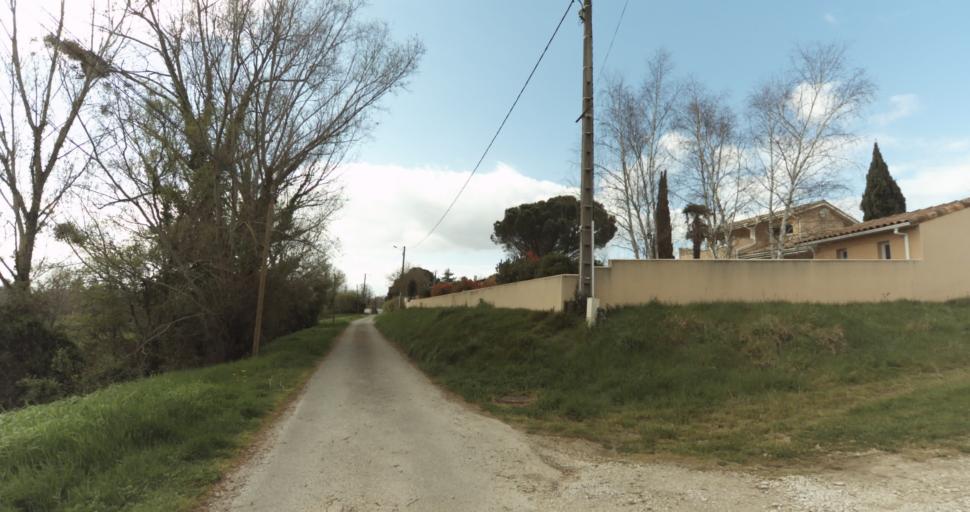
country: FR
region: Midi-Pyrenees
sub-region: Departement de la Haute-Garonne
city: Auterive
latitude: 43.3395
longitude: 1.4908
